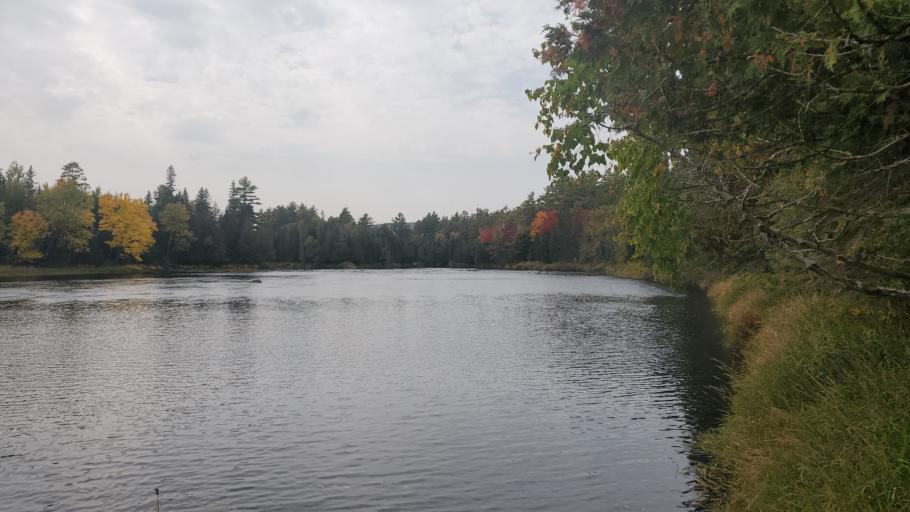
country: CA
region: Ontario
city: Renfrew
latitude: 45.2593
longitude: -77.1984
